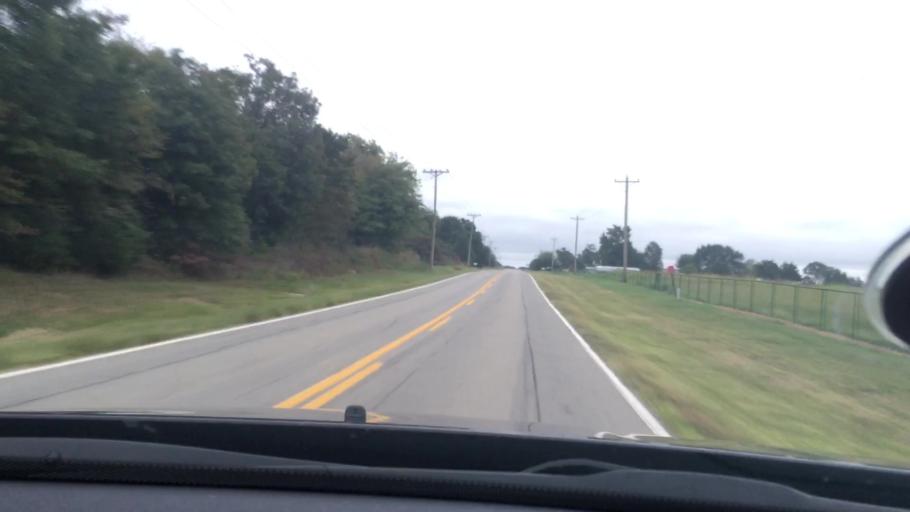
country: US
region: Oklahoma
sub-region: Sequoyah County
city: Vian
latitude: 35.6097
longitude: -94.9954
